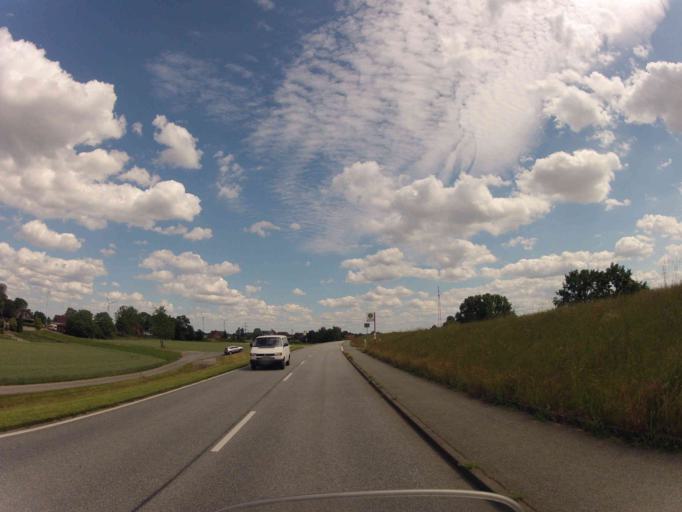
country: DE
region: Lower Saxony
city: Stelle
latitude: 53.4564
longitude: 10.0795
